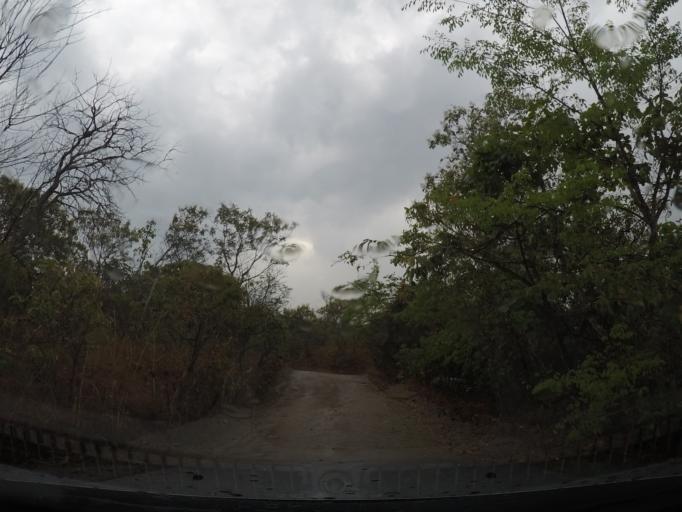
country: BR
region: Goias
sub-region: Pirenopolis
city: Pirenopolis
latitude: -15.8277
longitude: -48.8839
